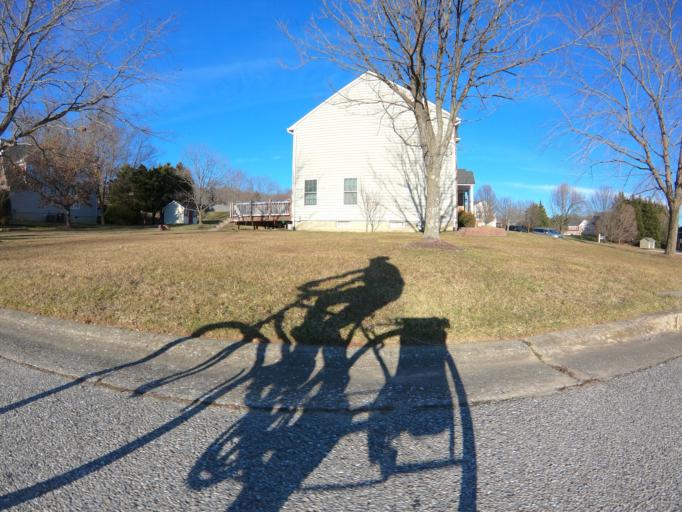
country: US
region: Maryland
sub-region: Howard County
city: West Elkridge
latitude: 39.2074
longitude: -76.7628
